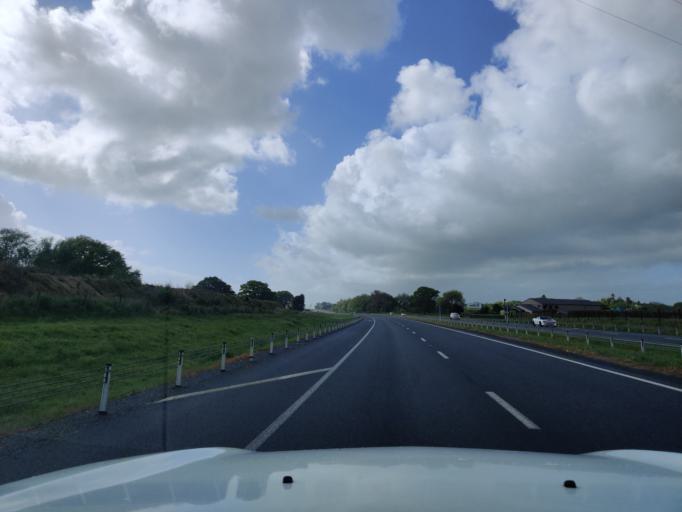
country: NZ
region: Waikato
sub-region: Waipa District
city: Cambridge
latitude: -37.8389
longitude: 175.3682
